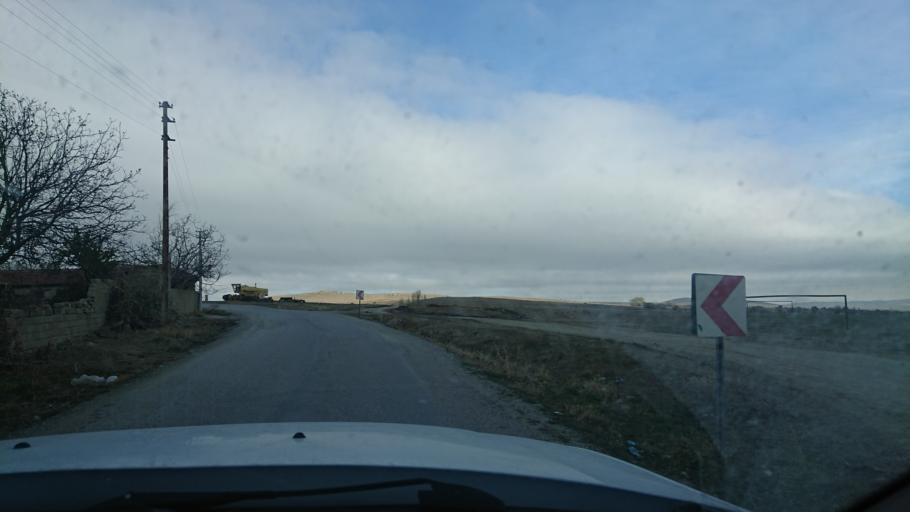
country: TR
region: Aksaray
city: Ortakoy
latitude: 38.7600
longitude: 34.0117
